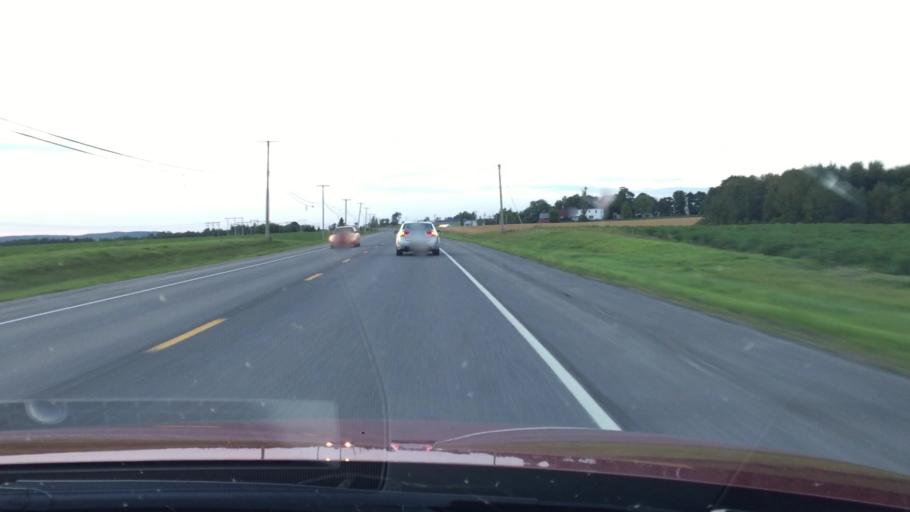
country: US
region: Maine
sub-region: Aroostook County
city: Easton
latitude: 46.4463
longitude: -67.8493
